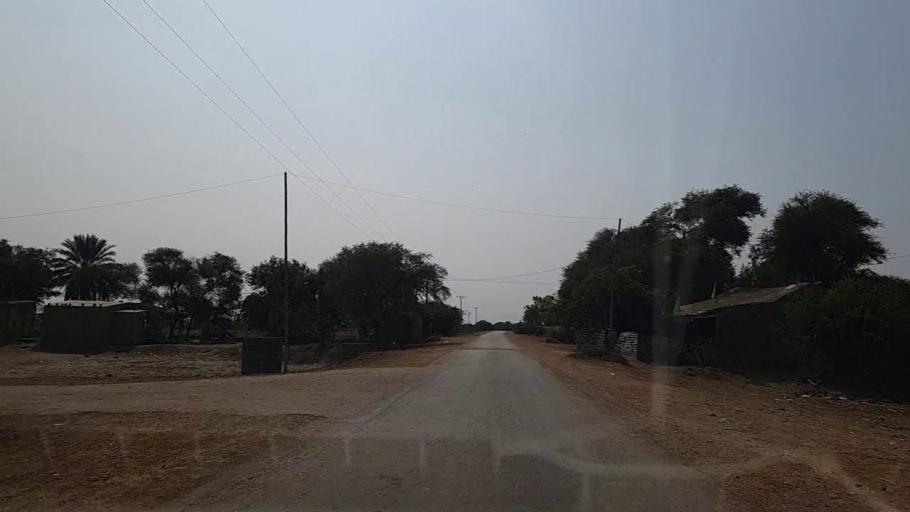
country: PK
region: Sindh
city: Chuhar Jamali
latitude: 24.3233
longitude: 67.9419
